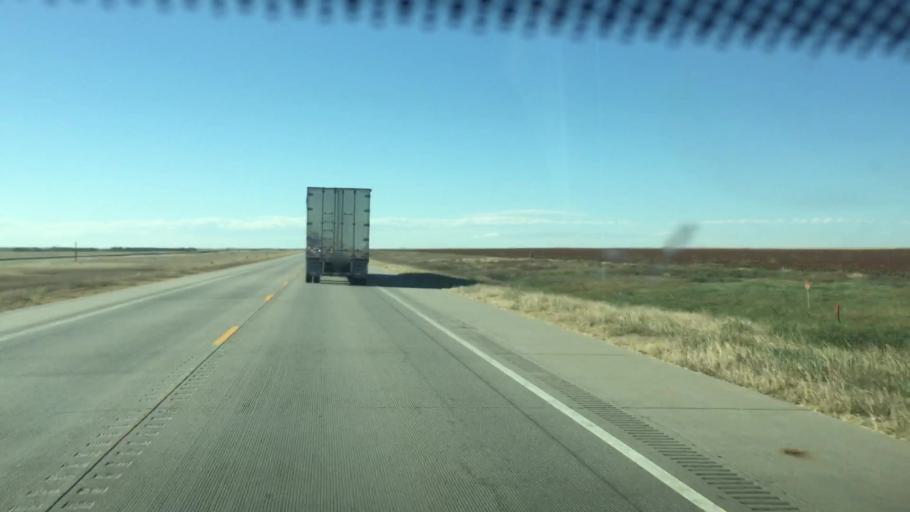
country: US
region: Colorado
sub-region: Kiowa County
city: Eads
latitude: 38.7954
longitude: -102.9452
